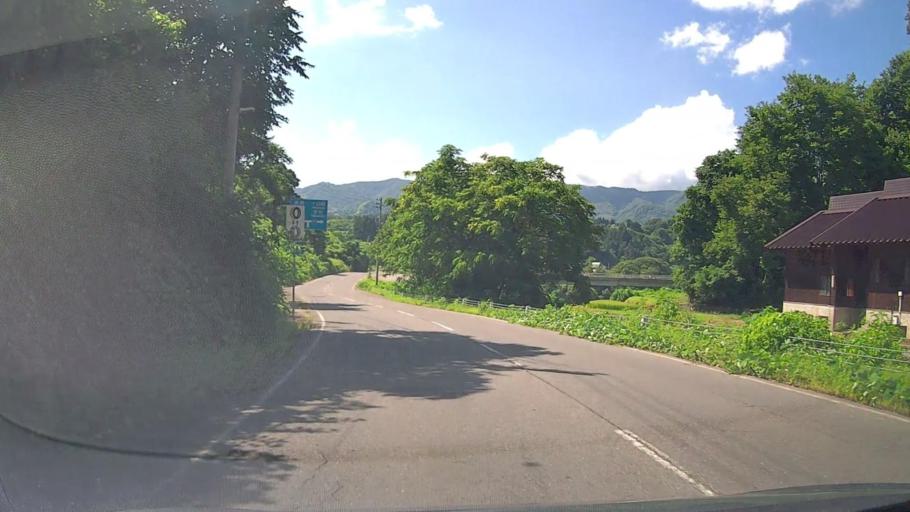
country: JP
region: Nagano
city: Iiyama
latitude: 36.9349
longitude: 138.4247
